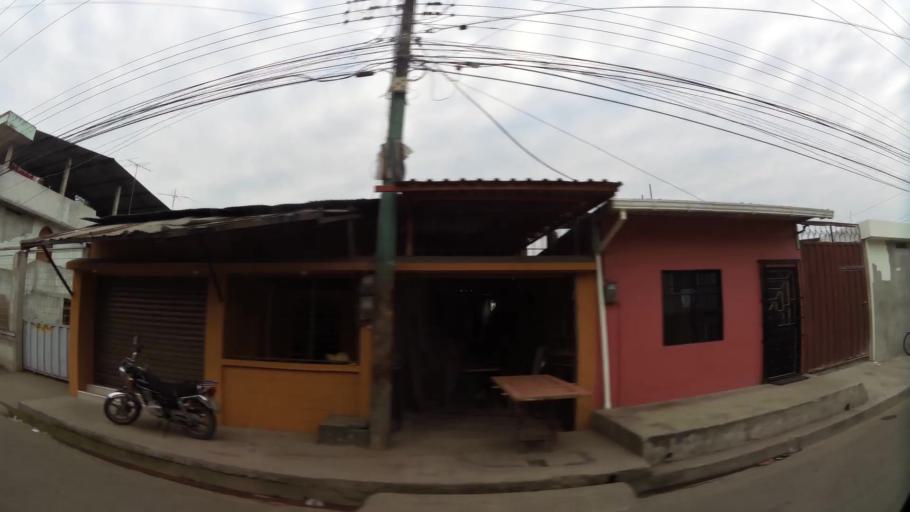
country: EC
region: El Oro
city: Machala
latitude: -3.2676
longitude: -79.9366
